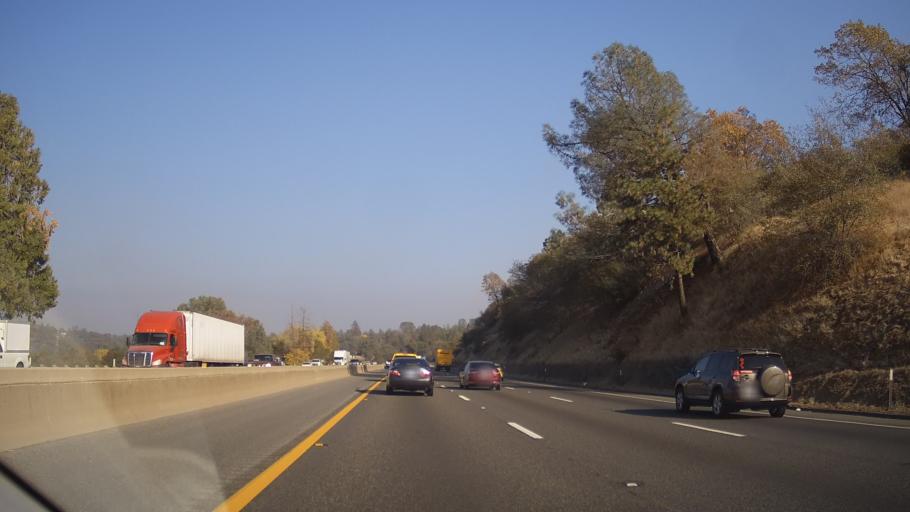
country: US
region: California
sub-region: Placer County
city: Newcastle
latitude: 38.8809
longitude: -121.1097
